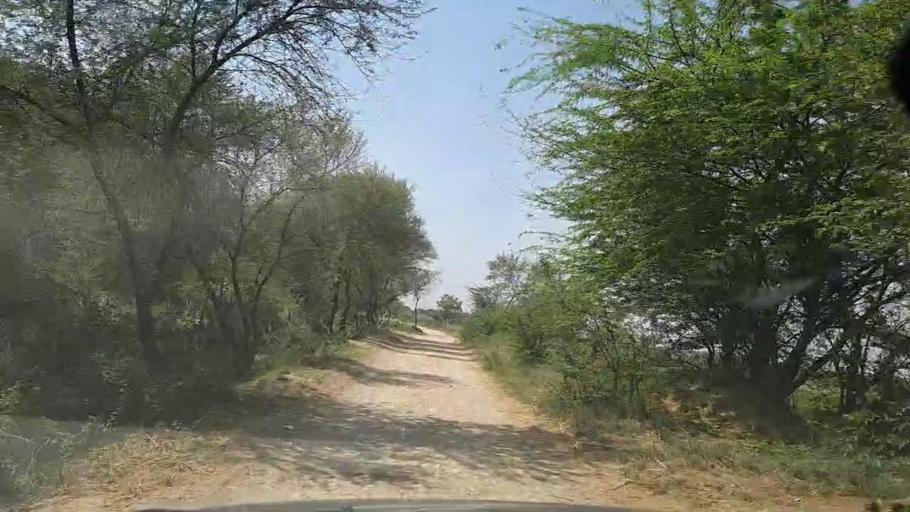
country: PK
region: Sindh
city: Mirpur Batoro
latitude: 24.6535
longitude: 68.1633
